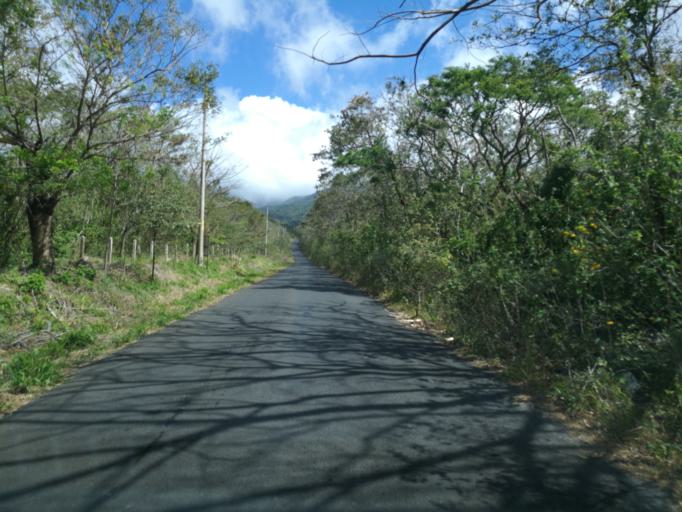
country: CR
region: Guanacaste
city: Liberia
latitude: 10.7643
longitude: -85.3530
